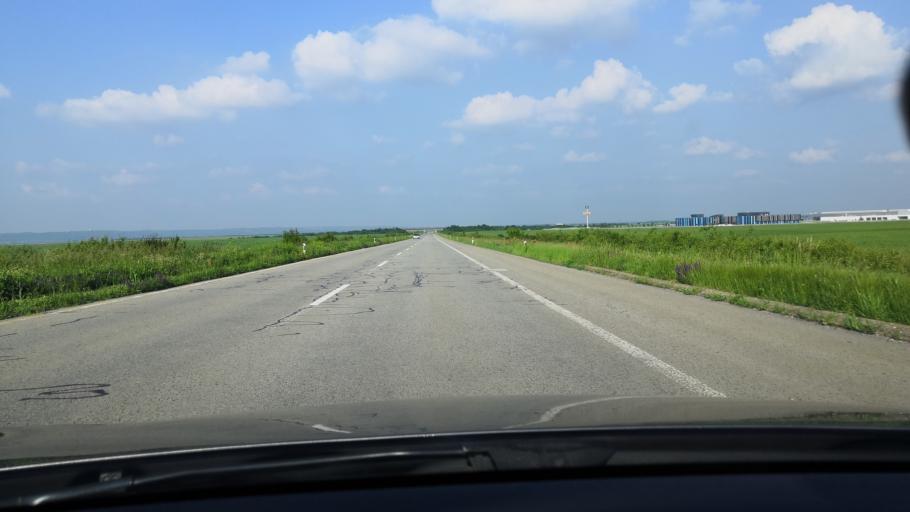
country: RS
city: Beska
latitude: 45.0955
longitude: 20.0805
